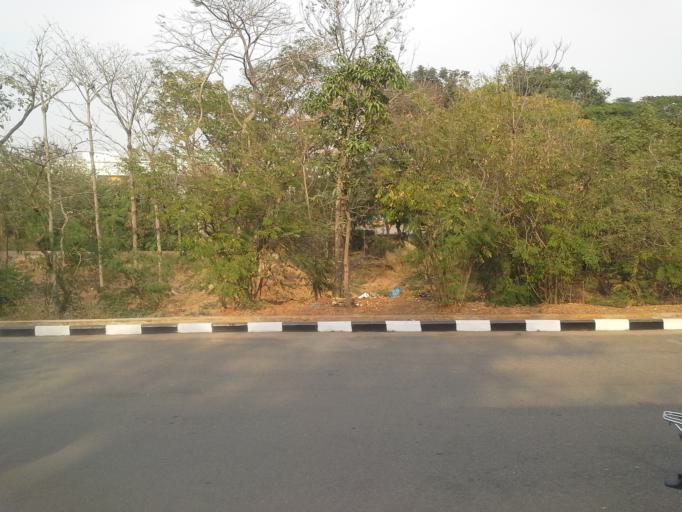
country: IN
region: Telangana
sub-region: Medak
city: Serilingampalle
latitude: 17.4460
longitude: 78.3506
